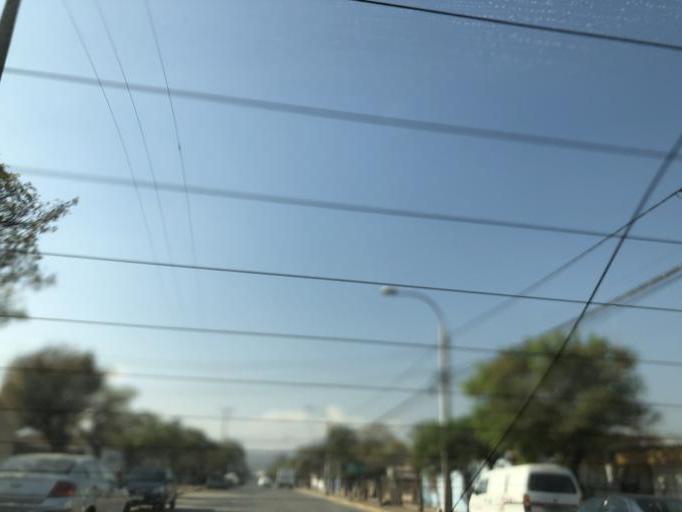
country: CL
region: Santiago Metropolitan
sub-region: Provincia de Cordillera
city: Puente Alto
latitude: -33.6067
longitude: -70.5663
